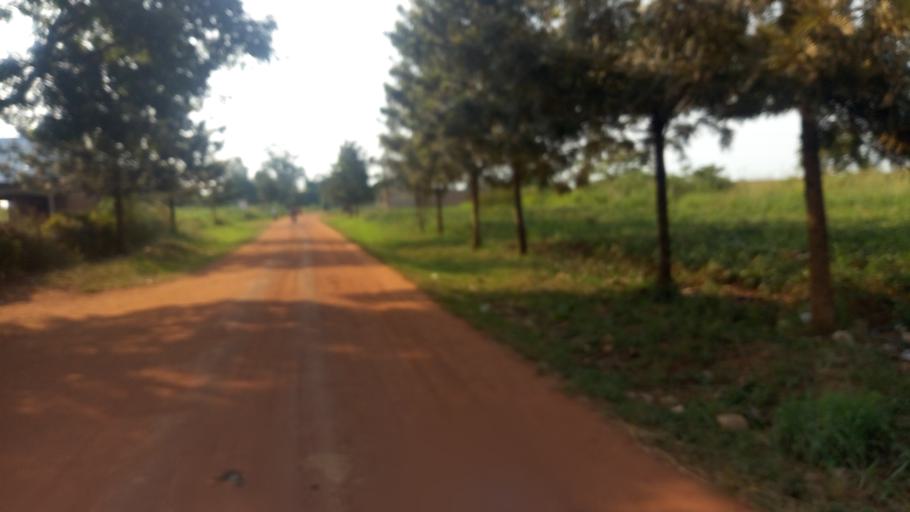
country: UG
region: Western Region
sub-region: Kiryandongo District
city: Kiryandongo
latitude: 1.8046
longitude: 32.0084
